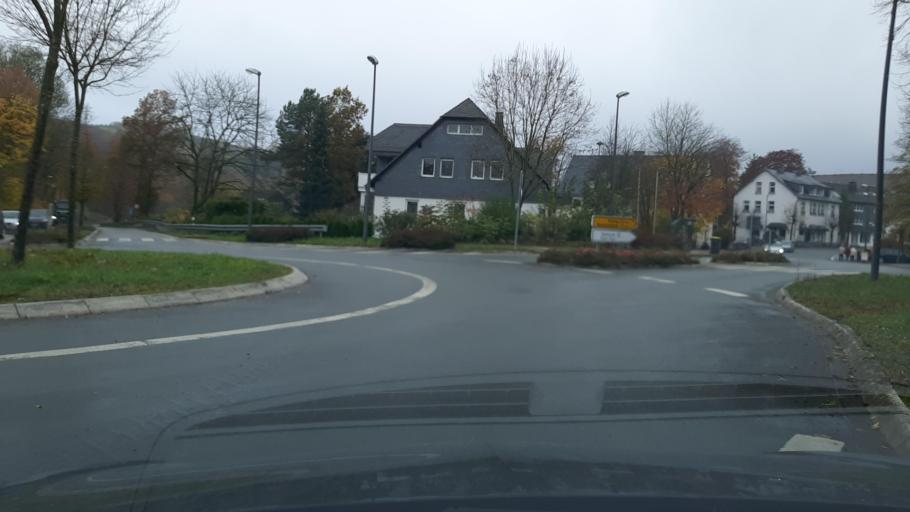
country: DE
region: North Rhine-Westphalia
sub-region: Regierungsbezirk Arnsberg
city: Bad Fredeburg
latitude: 51.1853
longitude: 8.3126
